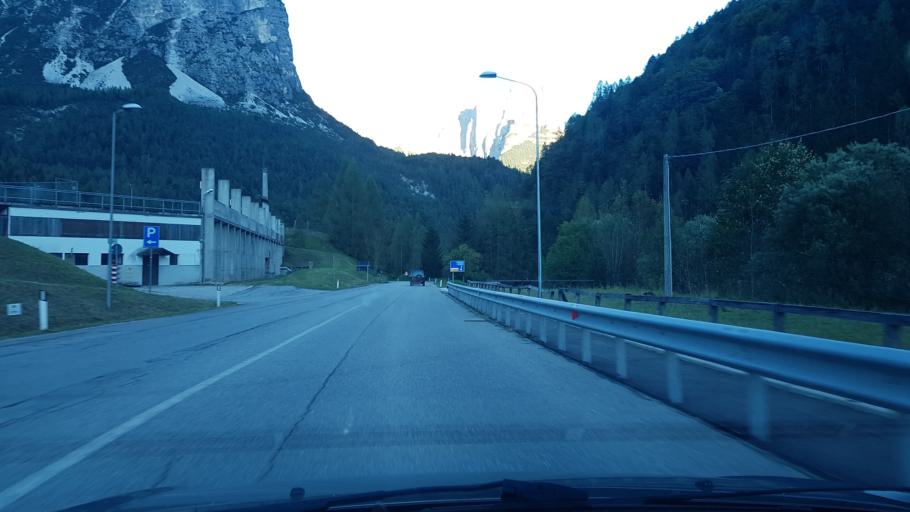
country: IT
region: Veneto
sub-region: Provincia di Belluno
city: Forno di Zoldo
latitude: 46.3457
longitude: 12.1874
